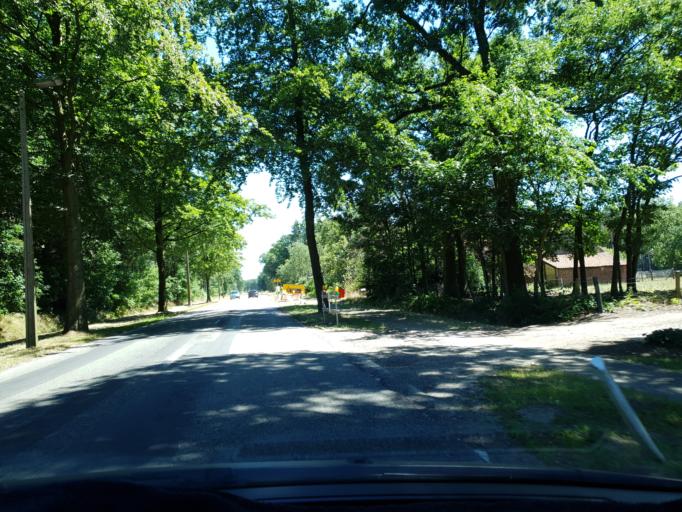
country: BE
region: Flanders
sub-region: Provincie Antwerpen
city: Olen
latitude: 51.1666
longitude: 4.8644
